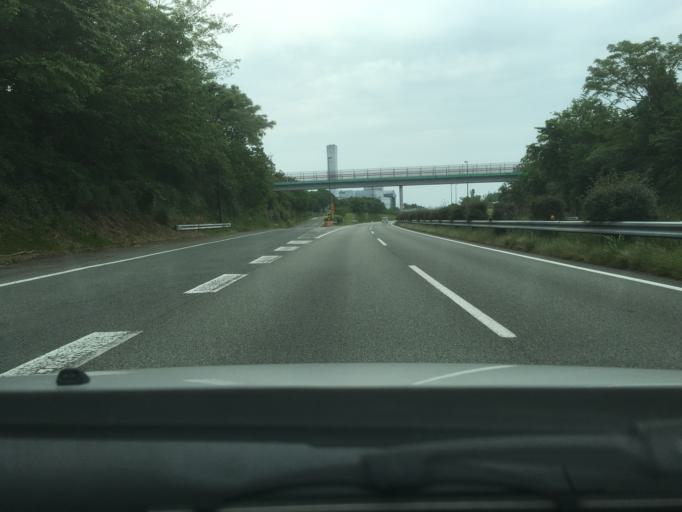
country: JP
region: Kumamoto
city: Ozu
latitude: 32.8120
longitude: 130.7933
